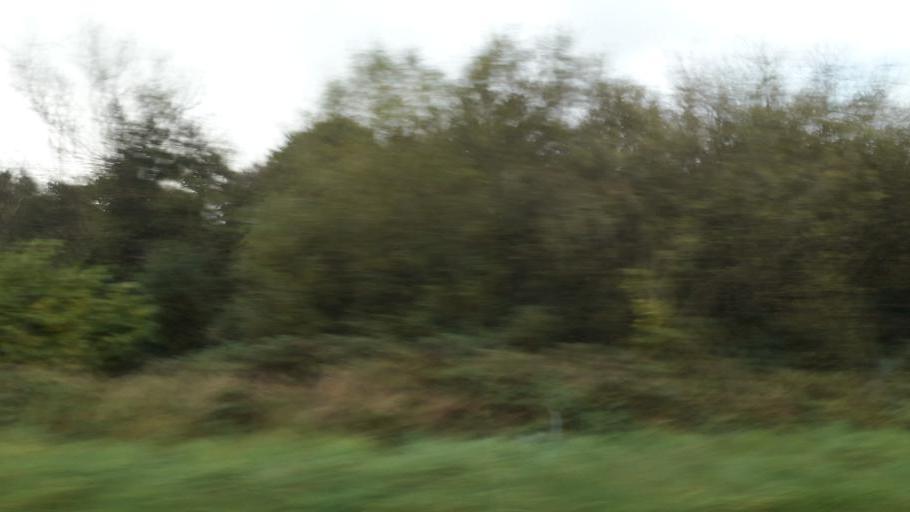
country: IE
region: Leinster
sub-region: An Longfort
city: Lanesborough
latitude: 53.7657
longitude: -8.0487
